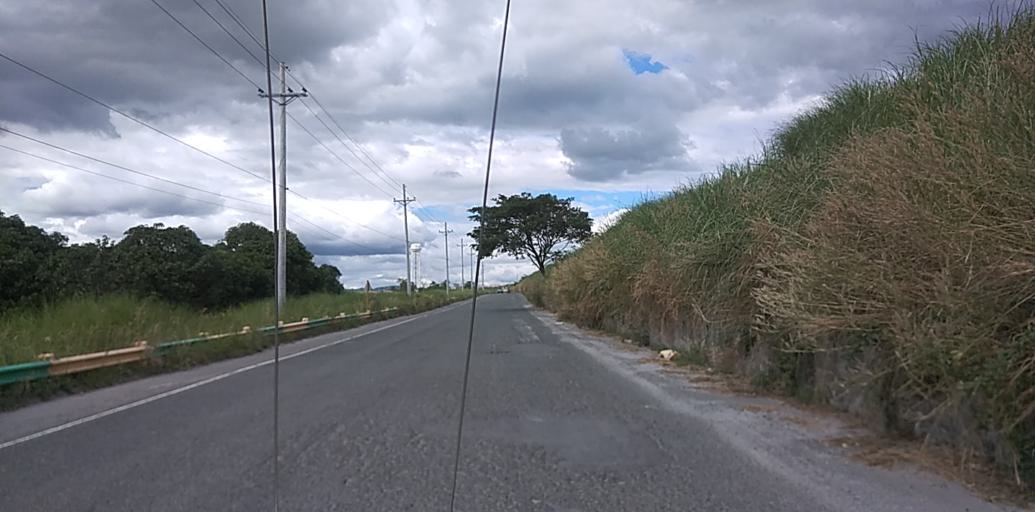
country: PH
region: Central Luzon
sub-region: Province of Pampanga
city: Dolores
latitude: 15.1073
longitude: 120.5200
